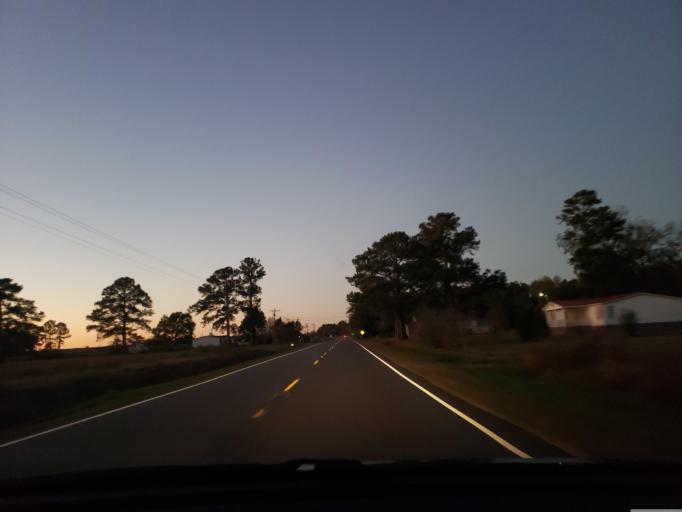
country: US
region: North Carolina
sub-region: Duplin County
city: Kenansville
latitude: 34.9130
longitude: -77.9299
